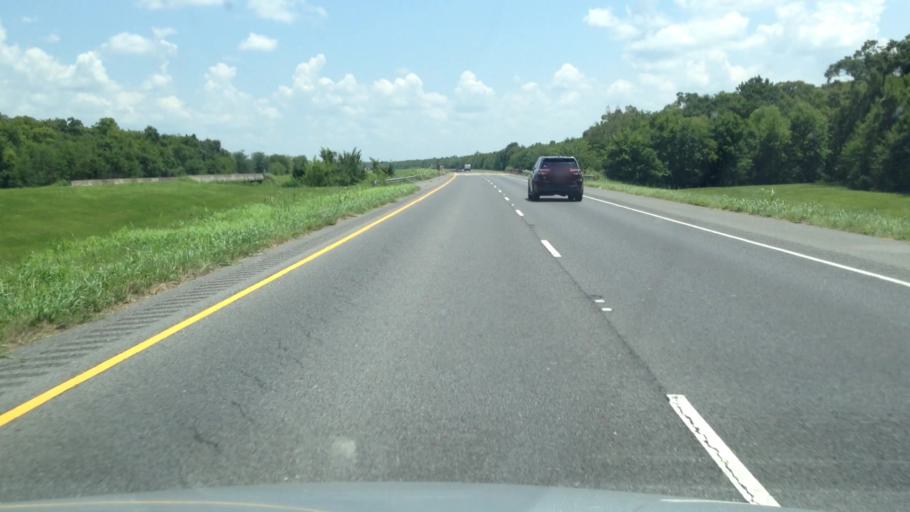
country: US
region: Louisiana
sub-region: Evangeline Parish
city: Ville Platte
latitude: 30.8131
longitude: -92.2190
